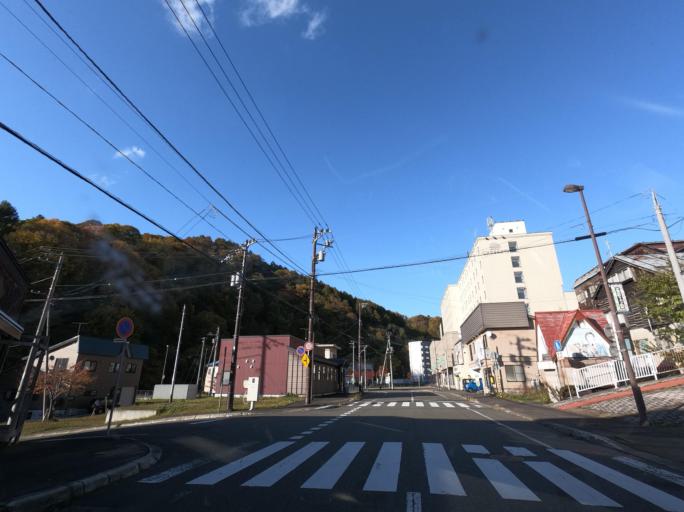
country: JP
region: Hokkaido
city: Iwamizawa
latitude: 43.0586
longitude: 141.9767
